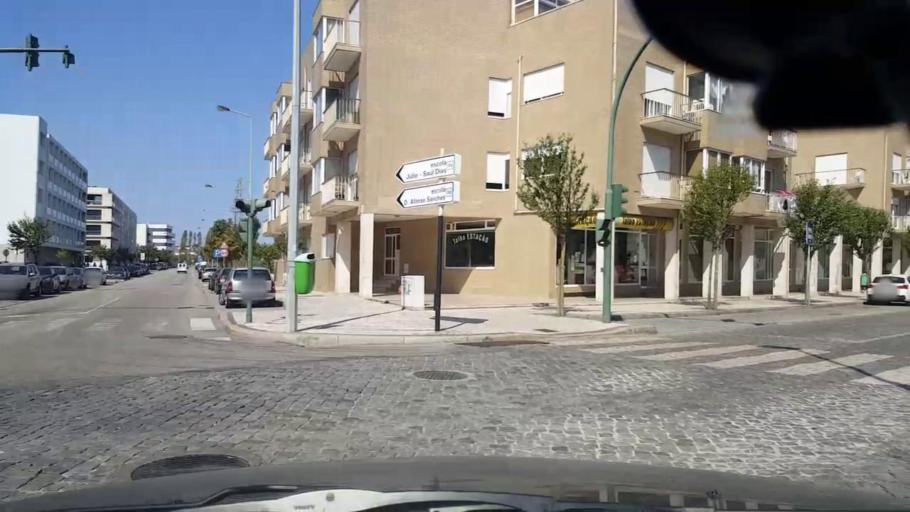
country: PT
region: Porto
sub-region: Vila do Conde
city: Vila do Conde
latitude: 41.3558
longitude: -8.7313
